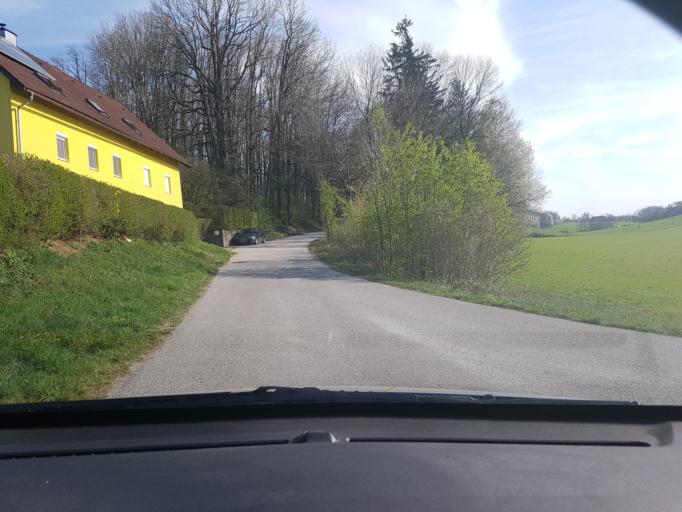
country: AT
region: Upper Austria
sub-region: Politischer Bezirk Linz-Land
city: Ansfelden
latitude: 48.1766
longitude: 14.3295
